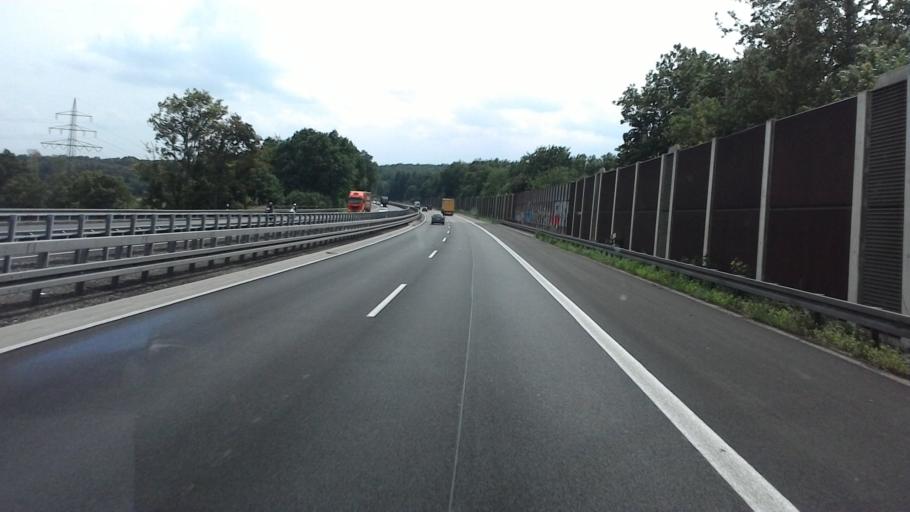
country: DE
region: North Rhine-Westphalia
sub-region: Regierungsbezirk Koln
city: Wurselen
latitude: 50.7942
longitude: 6.1694
